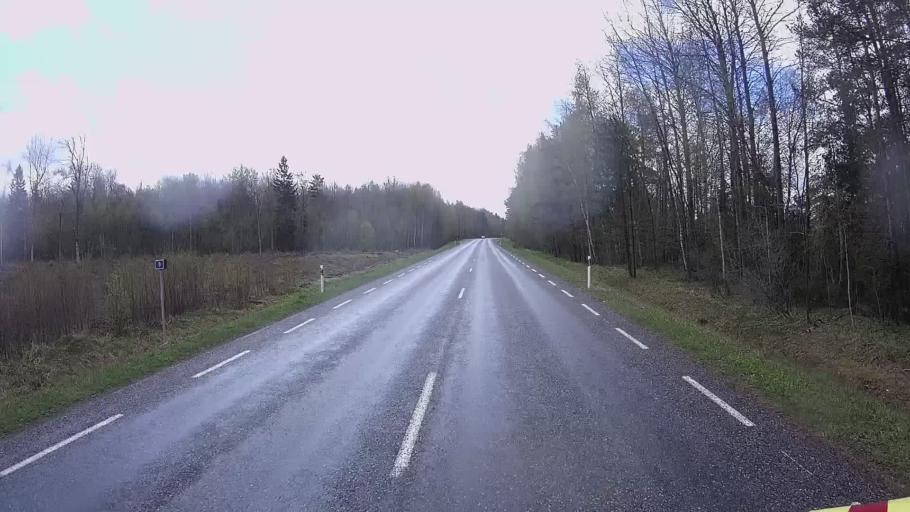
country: EE
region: Hiiumaa
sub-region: Kaerdla linn
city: Kardla
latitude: 58.9013
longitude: 22.9307
